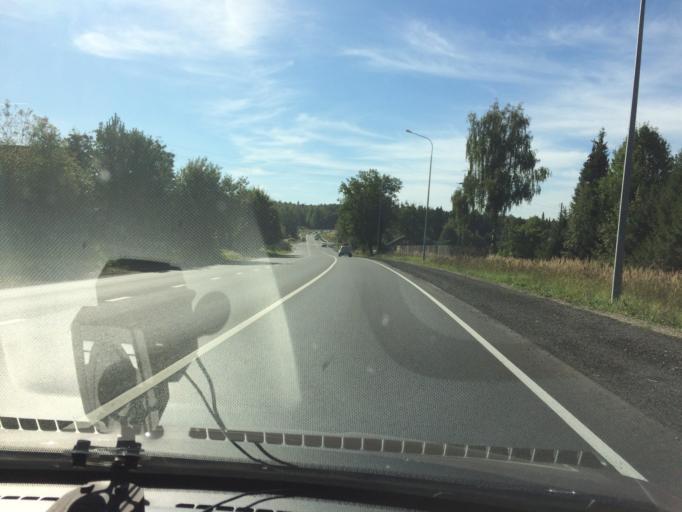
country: RU
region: Mariy-El
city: Yoshkar-Ola
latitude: 56.6005
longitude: 47.9712
